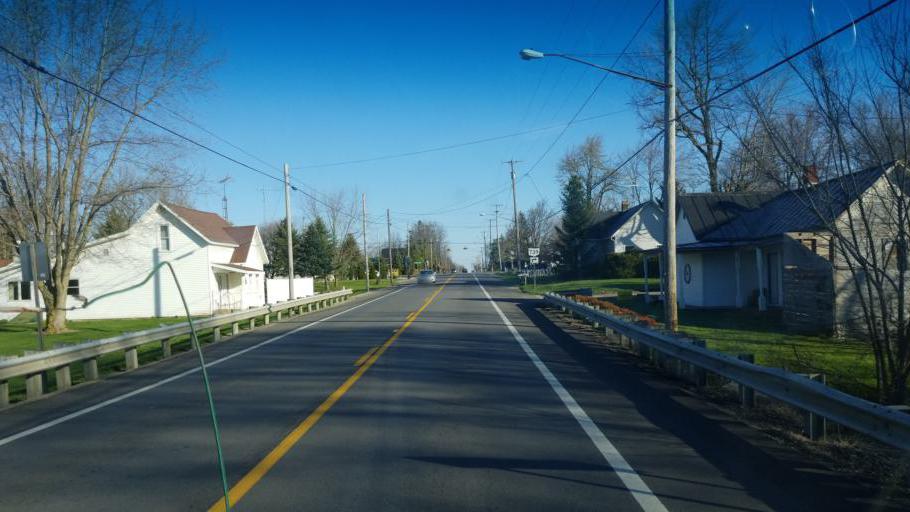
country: US
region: Ohio
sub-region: Union County
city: Richwood
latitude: 40.4525
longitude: -83.4545
